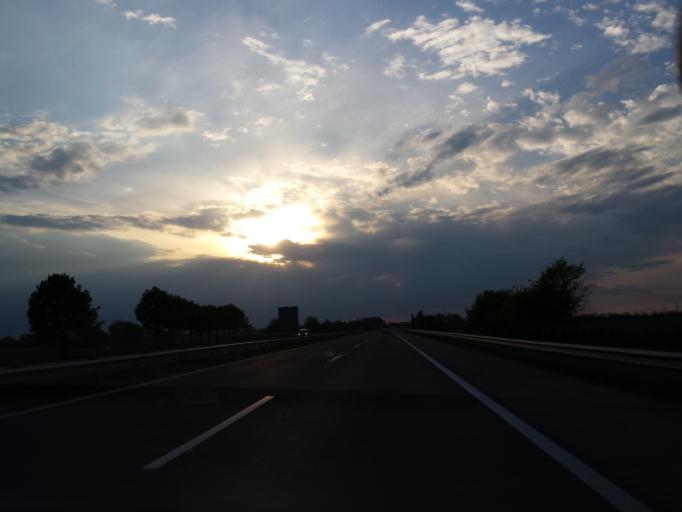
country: HU
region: Gyor-Moson-Sopron
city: Abda
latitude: 47.6894
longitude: 17.5285
